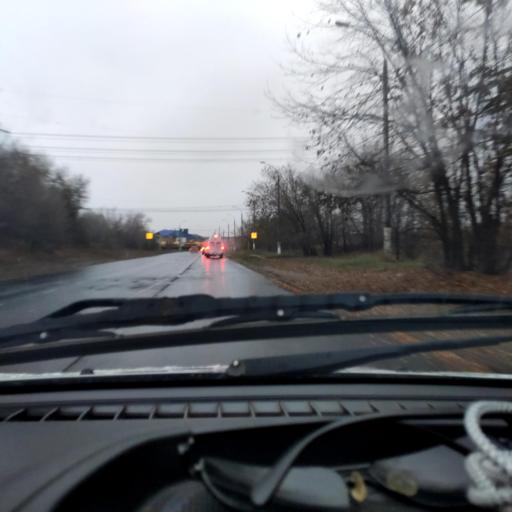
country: RU
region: Samara
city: Zhigulevsk
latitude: 53.4817
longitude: 49.5028
